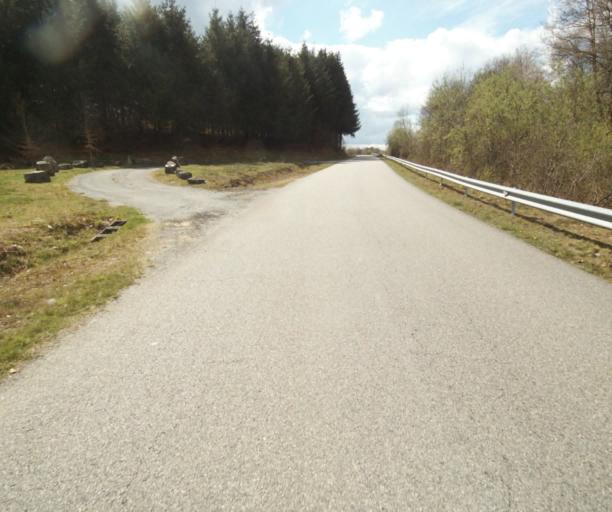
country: FR
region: Limousin
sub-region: Departement de la Correze
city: Correze
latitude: 45.2995
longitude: 1.8924
